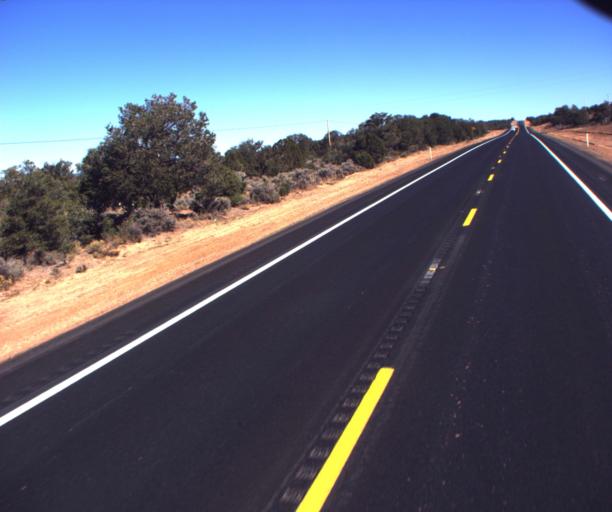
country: US
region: Arizona
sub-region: Apache County
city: Ganado
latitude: 35.7182
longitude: -109.3930
